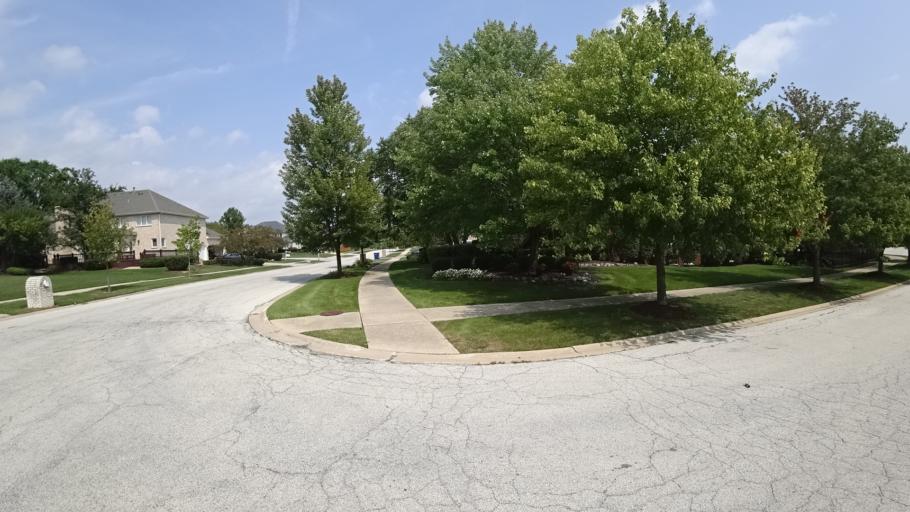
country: US
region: Illinois
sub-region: Cook County
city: Orland Park
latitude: 41.6349
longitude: -87.8869
